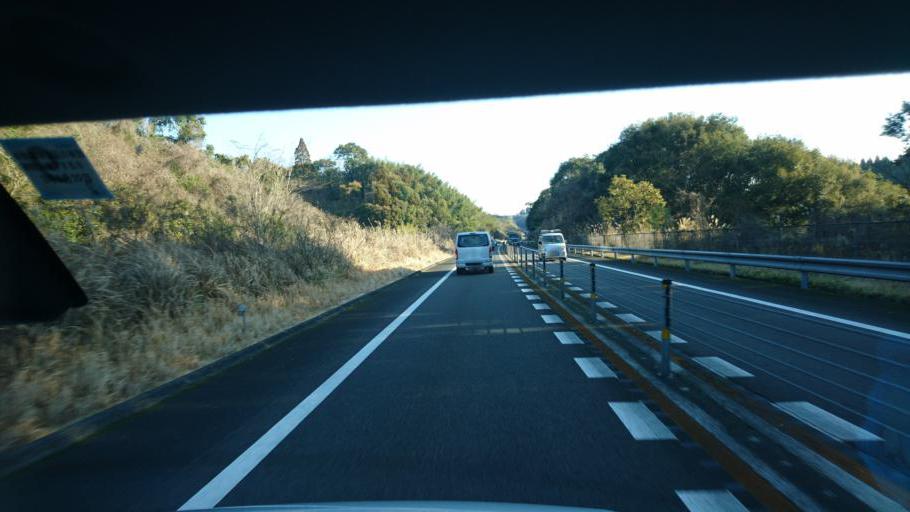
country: JP
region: Miyazaki
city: Tsuma
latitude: 32.0130
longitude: 131.3820
